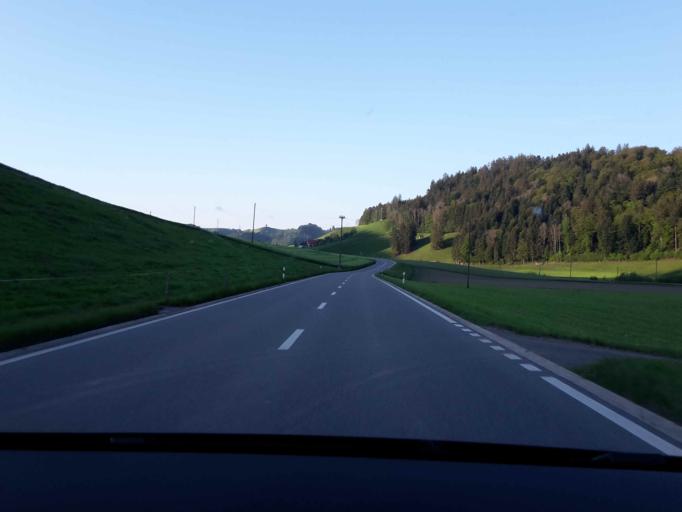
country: CH
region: Bern
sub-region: Emmental District
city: Lutzelfluh
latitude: 46.9893
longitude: 7.6531
